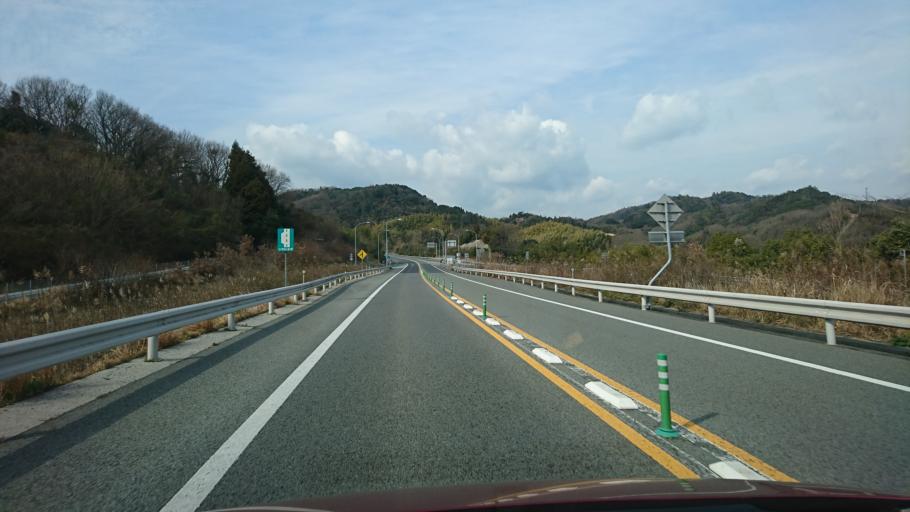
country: JP
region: Hiroshima
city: Innoshima
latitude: 34.1291
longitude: 133.0332
